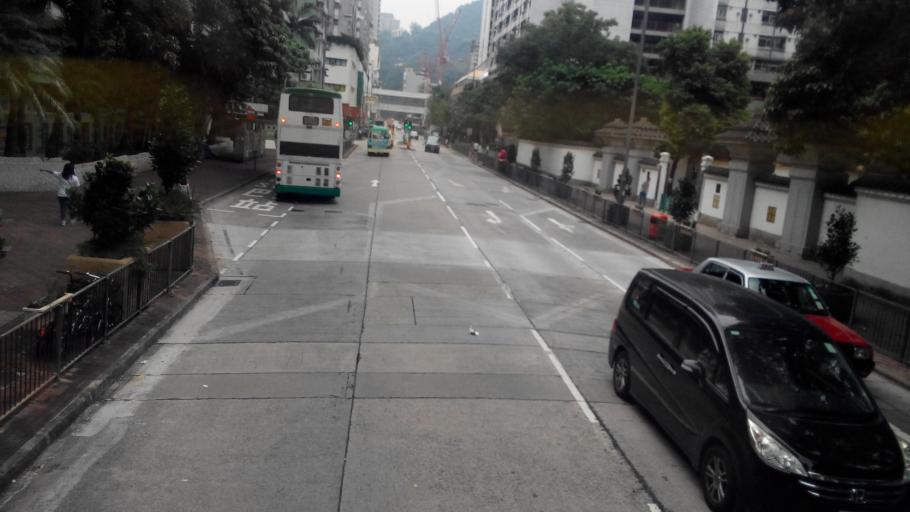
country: HK
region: Sham Shui Po
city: Sham Shui Po
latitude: 22.3374
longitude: 114.1596
